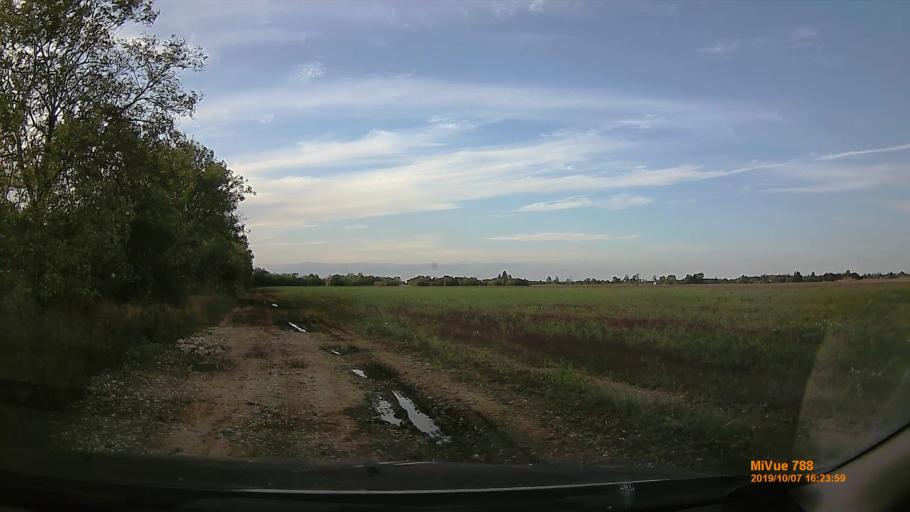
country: HU
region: Bekes
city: Szarvas
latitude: 46.8155
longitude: 20.6321
